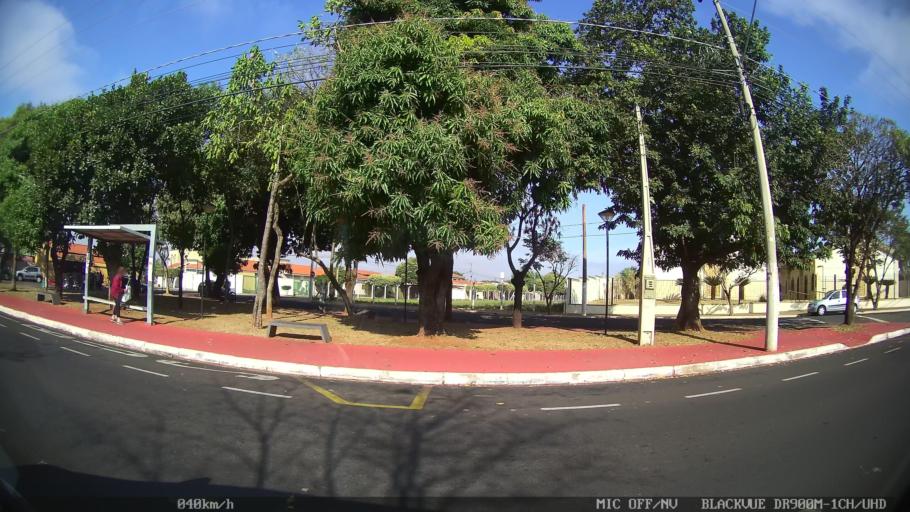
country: BR
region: Sao Paulo
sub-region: Sao Jose Do Rio Preto
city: Sao Jose do Rio Preto
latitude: -20.7956
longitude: -49.4138
